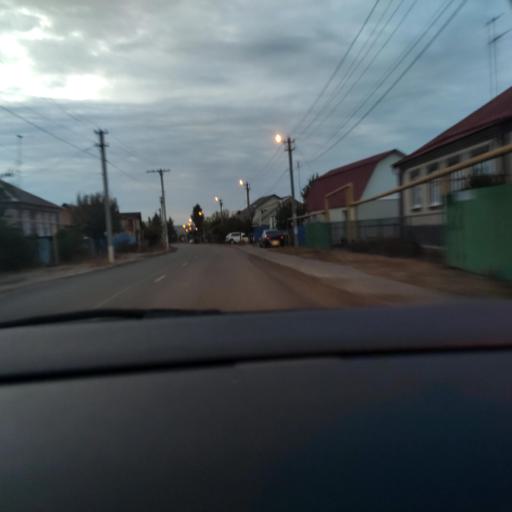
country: RU
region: Voronezj
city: Podgornoye
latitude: 51.7262
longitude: 39.1425
